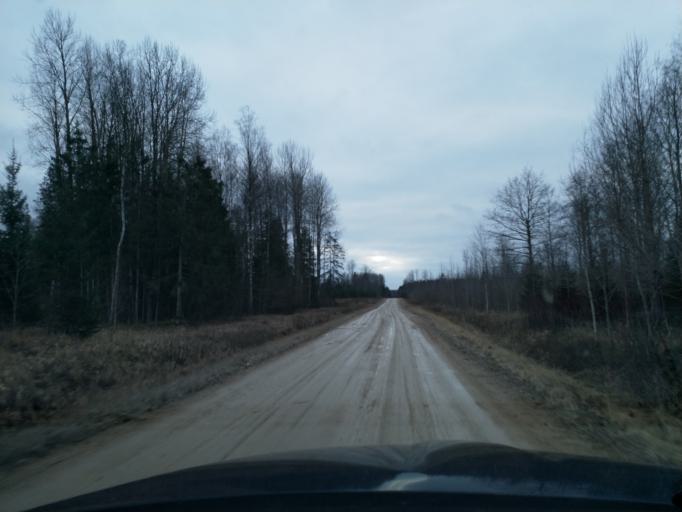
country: LV
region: Kuldigas Rajons
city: Kuldiga
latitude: 56.9099
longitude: 22.2646
